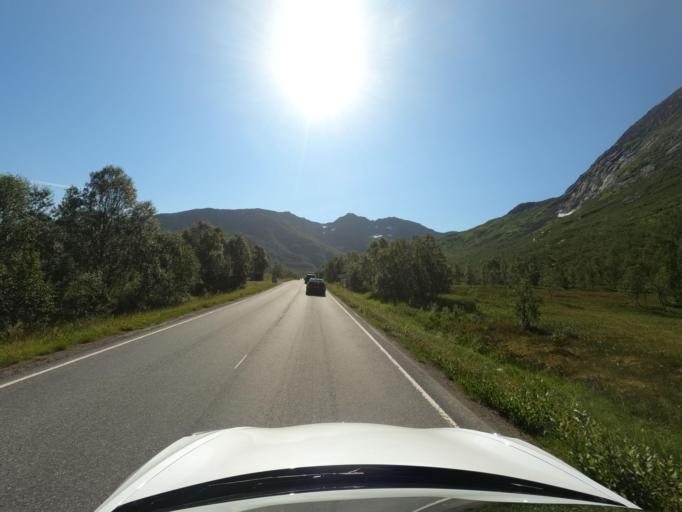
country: NO
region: Nordland
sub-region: Lodingen
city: Lodingen
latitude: 68.5322
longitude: 15.7251
